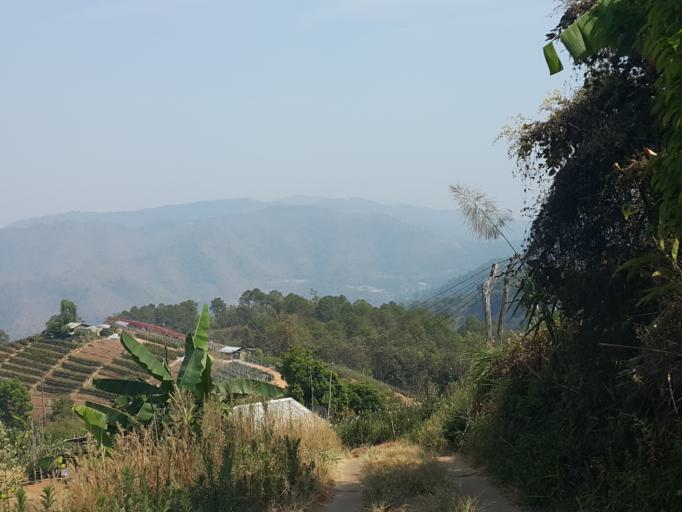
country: TH
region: Chiang Mai
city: Samoeng
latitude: 18.8844
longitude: 98.7948
